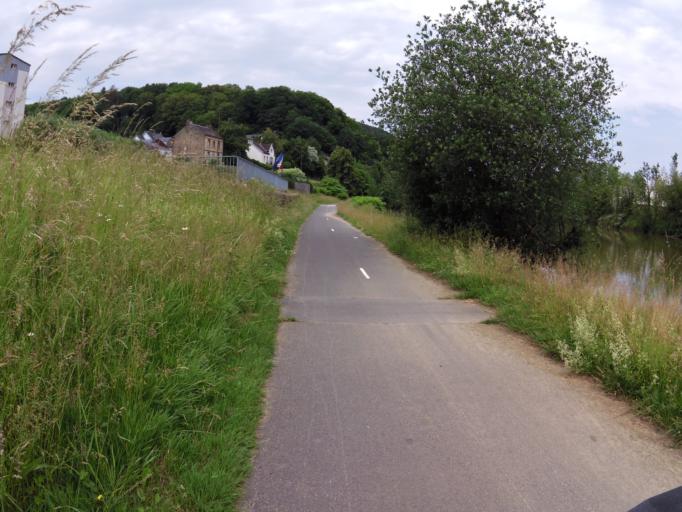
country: FR
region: Champagne-Ardenne
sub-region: Departement des Ardennes
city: Nouzonville
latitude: 49.8124
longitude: 4.7398
